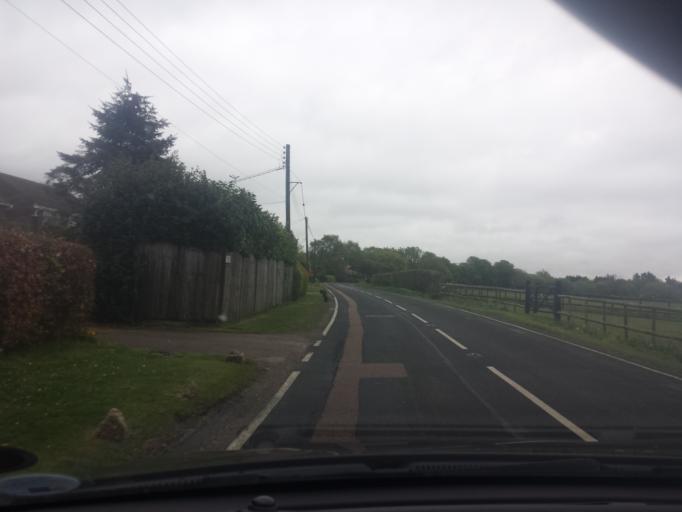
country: GB
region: England
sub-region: Suffolk
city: Shotley Gate
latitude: 51.9355
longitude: 1.1952
